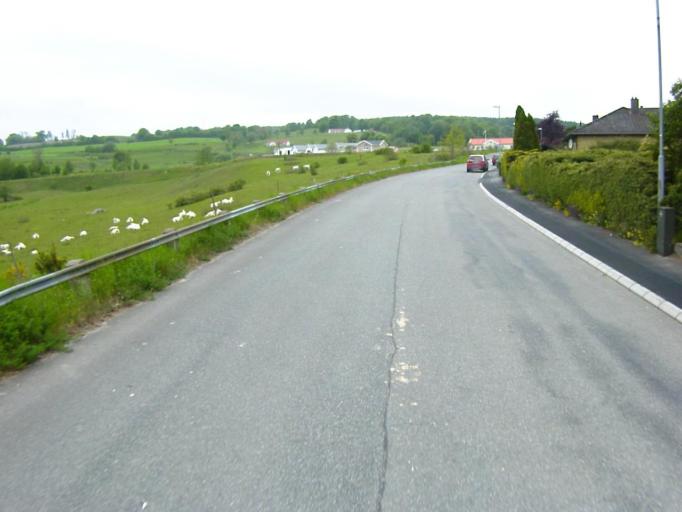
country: SE
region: Skane
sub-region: Kristianstads Kommun
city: Degeberga
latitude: 55.8378
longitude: 14.0837
